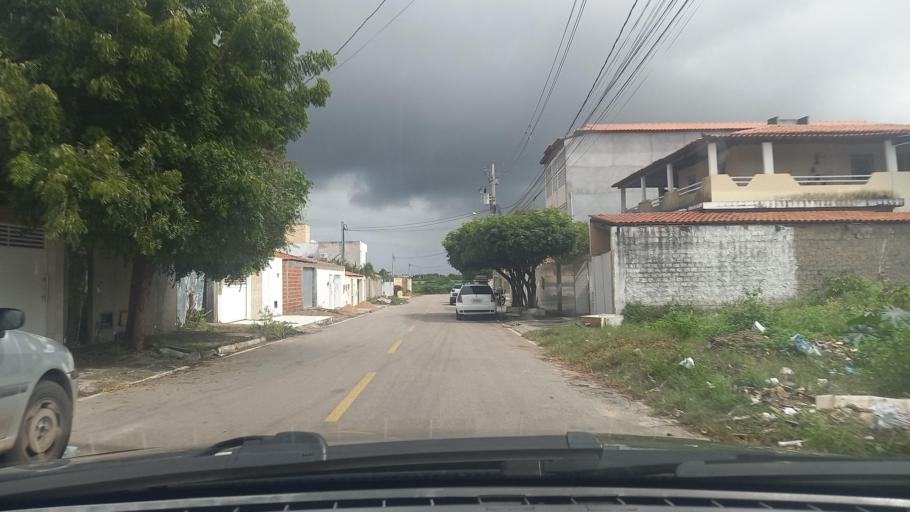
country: BR
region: Bahia
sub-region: Paulo Afonso
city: Paulo Afonso
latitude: -9.4005
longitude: -38.2443
